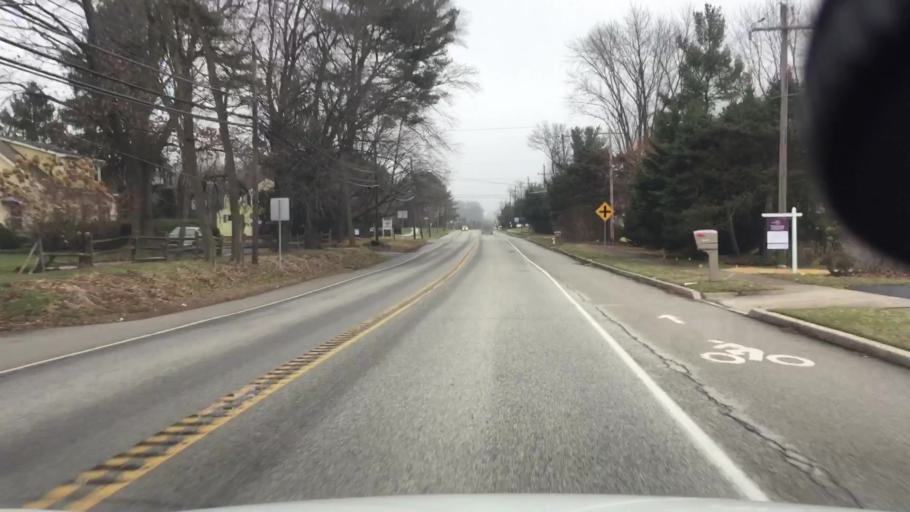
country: US
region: Pennsylvania
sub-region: Montgomery County
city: Dresher
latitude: 40.1532
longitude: -75.1874
